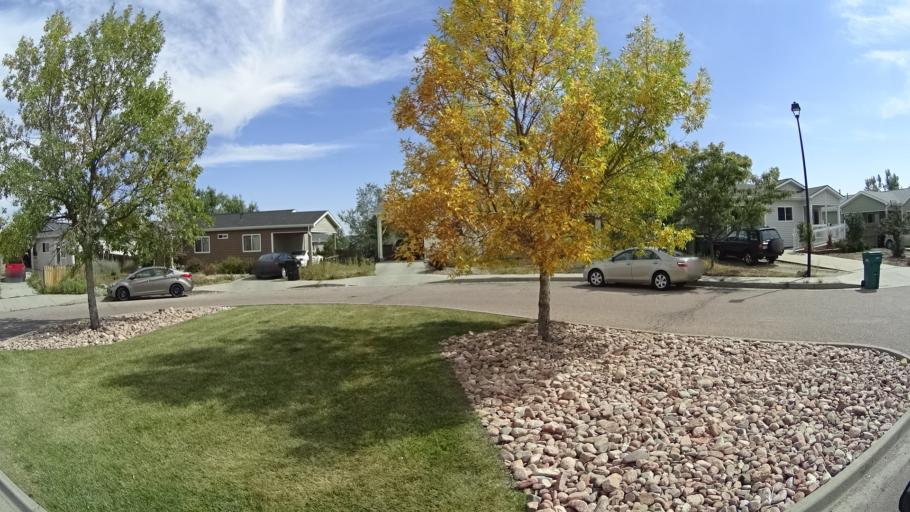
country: US
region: Colorado
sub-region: El Paso County
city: Cimarron Hills
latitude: 38.9080
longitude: -104.7121
